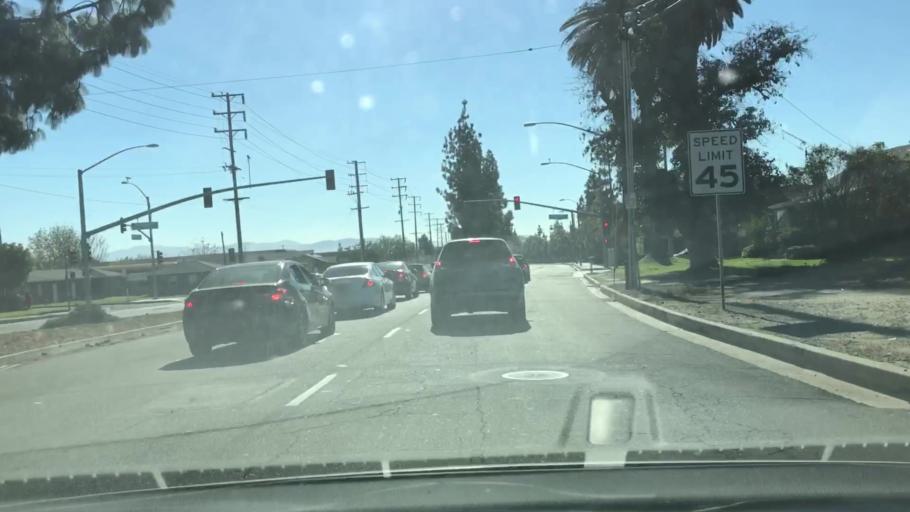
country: US
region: California
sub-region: San Bernardino County
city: Montclair
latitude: 34.0528
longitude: -117.6895
